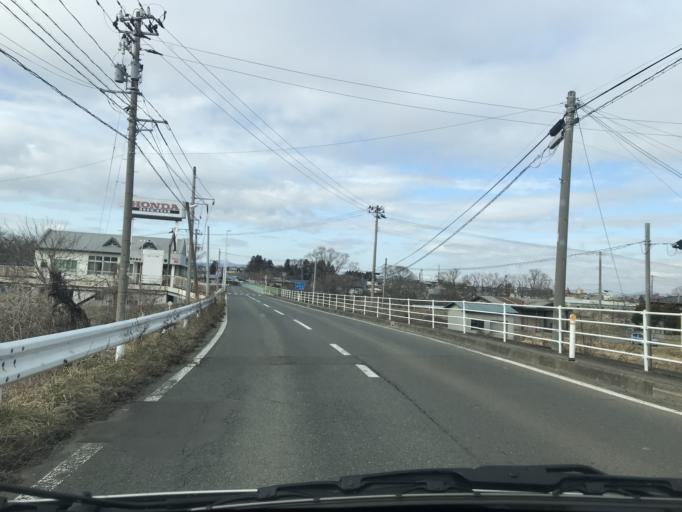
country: JP
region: Iwate
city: Hanamaki
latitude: 39.3774
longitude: 141.1068
